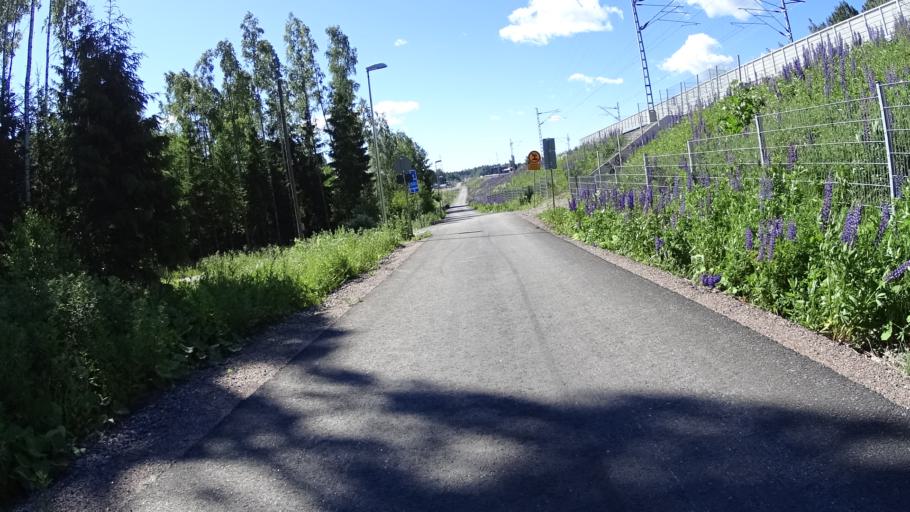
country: FI
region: Uusimaa
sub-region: Helsinki
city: Kilo
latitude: 60.2989
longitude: 24.8429
